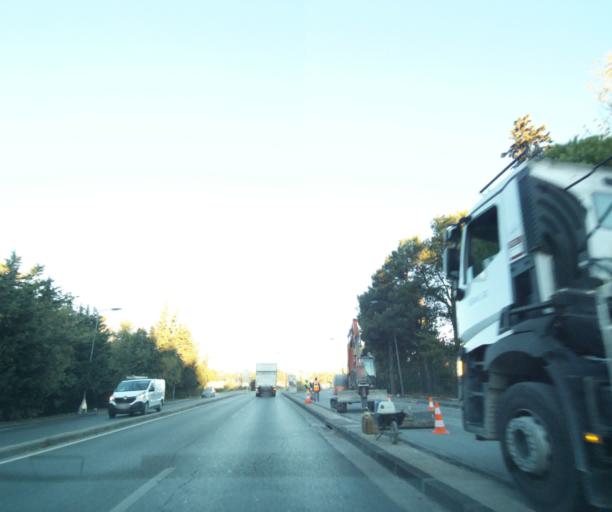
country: FR
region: Provence-Alpes-Cote d'Azur
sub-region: Departement des Bouches-du-Rhone
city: Allauch
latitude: 43.3052
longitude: 5.4710
